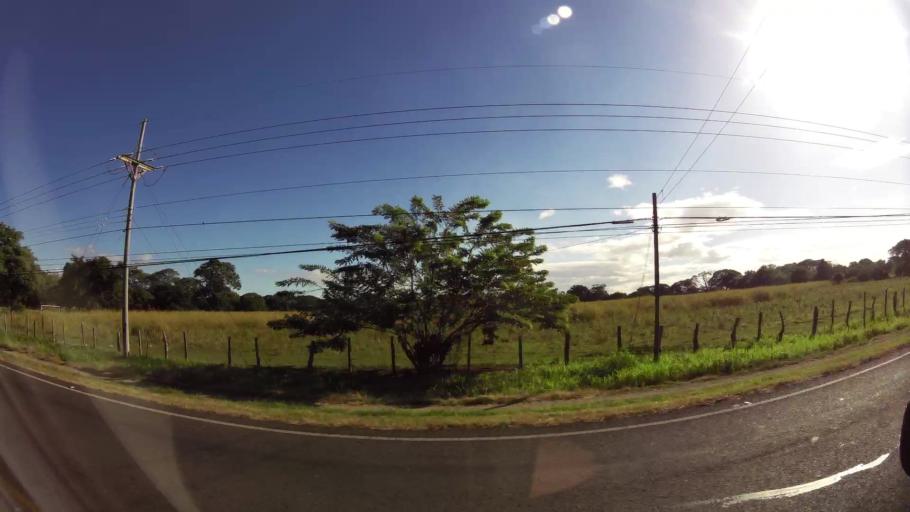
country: CR
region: Guanacaste
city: Belen
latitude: 10.4762
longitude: -85.5636
